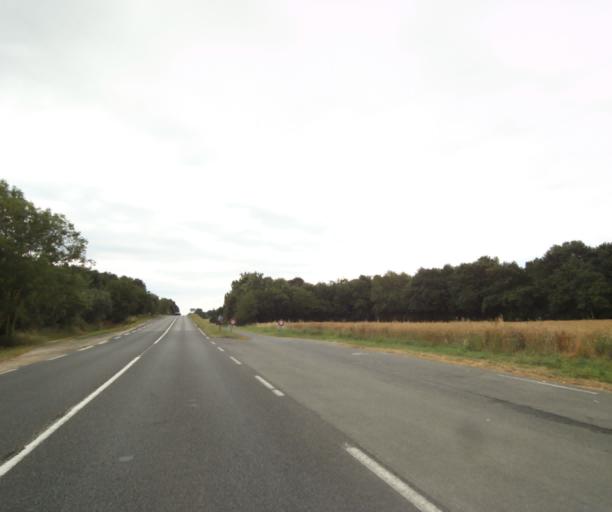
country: FR
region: Ile-de-France
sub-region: Departement de Seine-et-Marne
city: Cely
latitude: 48.4657
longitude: 2.5377
